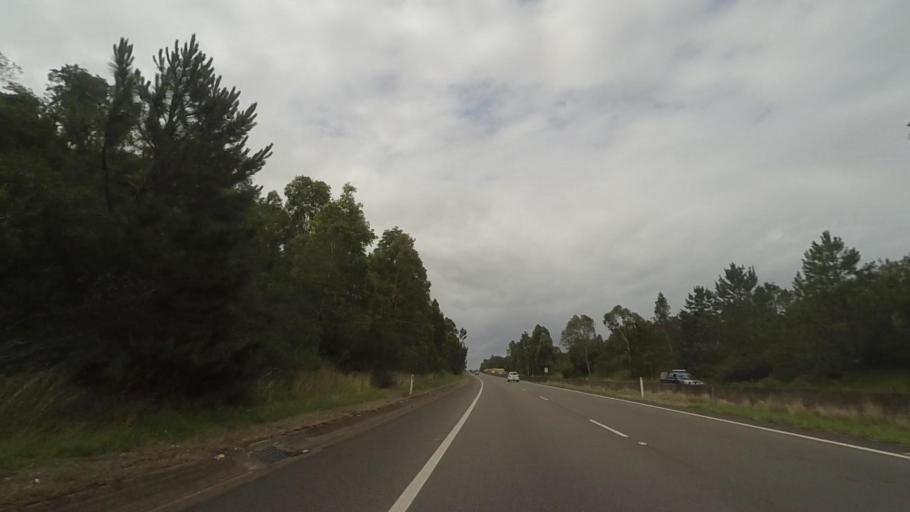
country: AU
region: New South Wales
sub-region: Port Stephens Shire
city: Raymond Terrace
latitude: -32.7671
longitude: 151.7627
